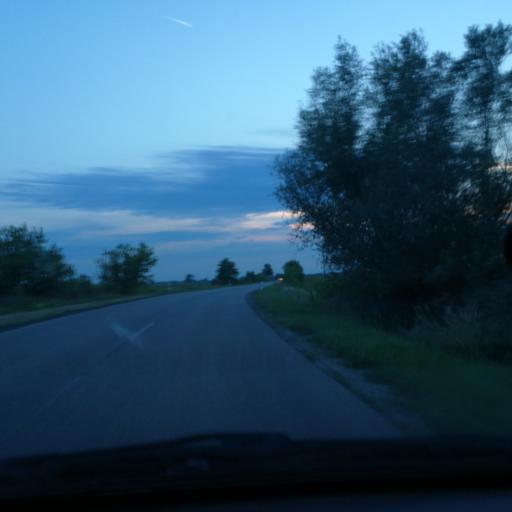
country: HU
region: Bacs-Kiskun
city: Kalocsa
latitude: 46.5090
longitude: 19.0871
